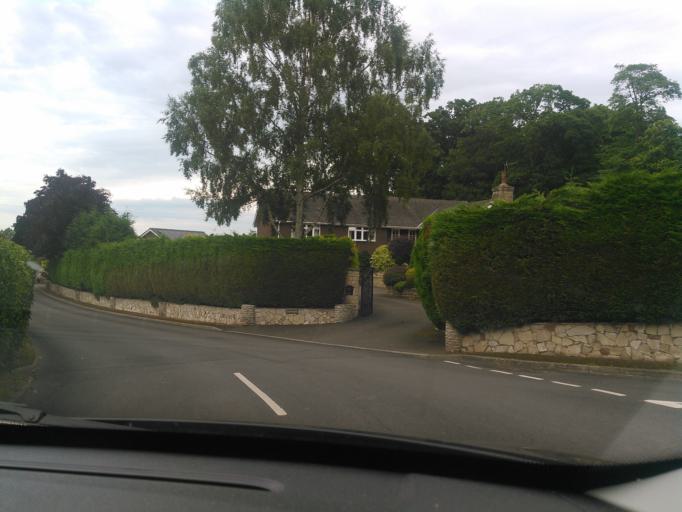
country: GB
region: England
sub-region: Shropshire
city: Prees
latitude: 52.8552
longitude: -2.6463
